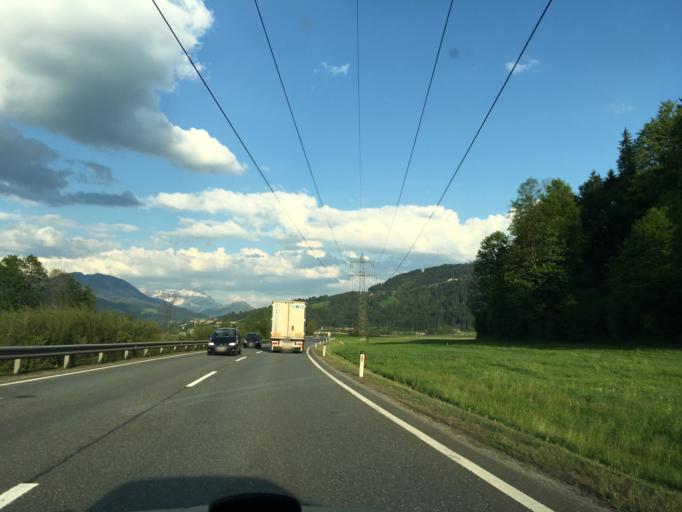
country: AT
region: Tyrol
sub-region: Politischer Bezirk Kitzbuhel
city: Oberndorf in Tirol
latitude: 47.5217
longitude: 12.3936
